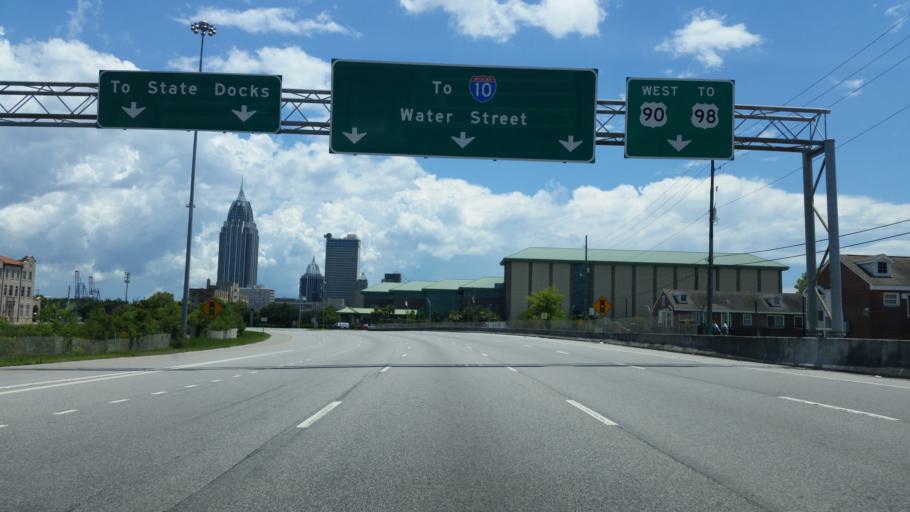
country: US
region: Alabama
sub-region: Mobile County
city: Mobile
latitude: 30.7015
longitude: -88.0475
